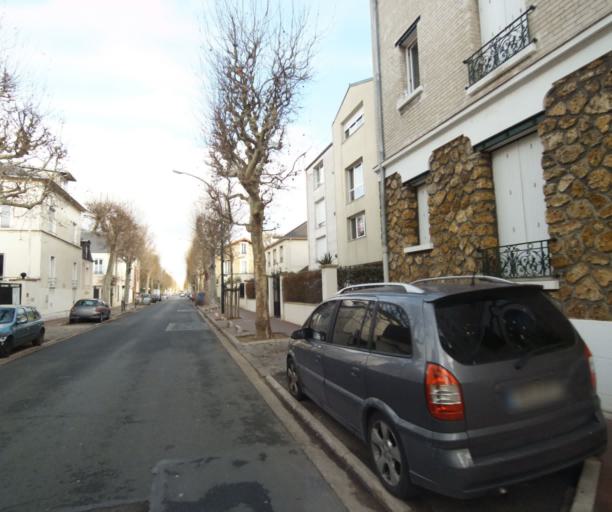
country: FR
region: Ile-de-France
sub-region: Departement des Hauts-de-Seine
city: La Garenne-Colombes
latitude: 48.9028
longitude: 2.2437
